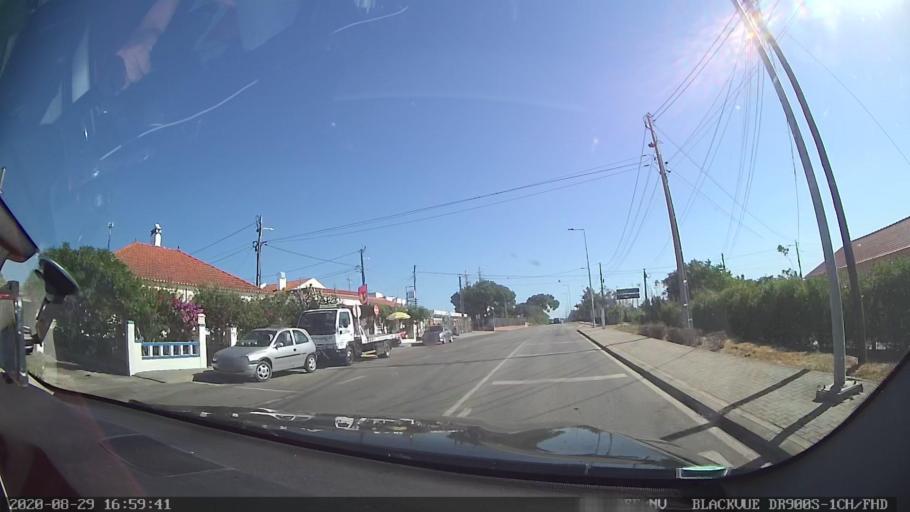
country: PT
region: Setubal
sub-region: Alcacer do Sal
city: Alcacer do Sal
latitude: 38.3855
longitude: -8.5130
